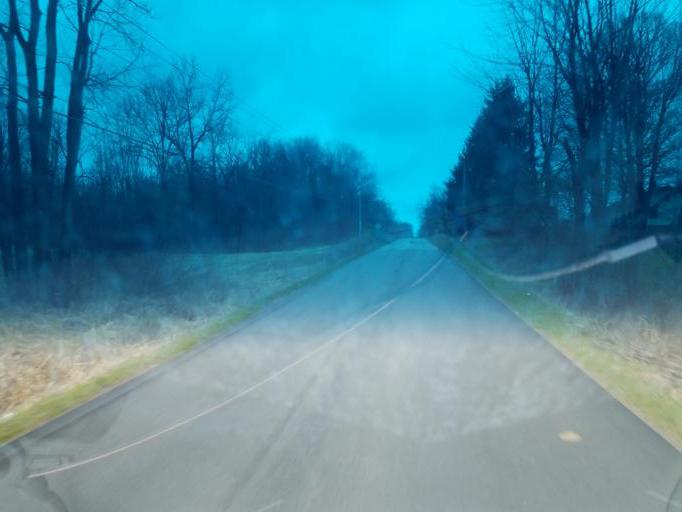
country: US
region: Ohio
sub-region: Morrow County
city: Mount Gilead
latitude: 40.4255
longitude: -82.7865
